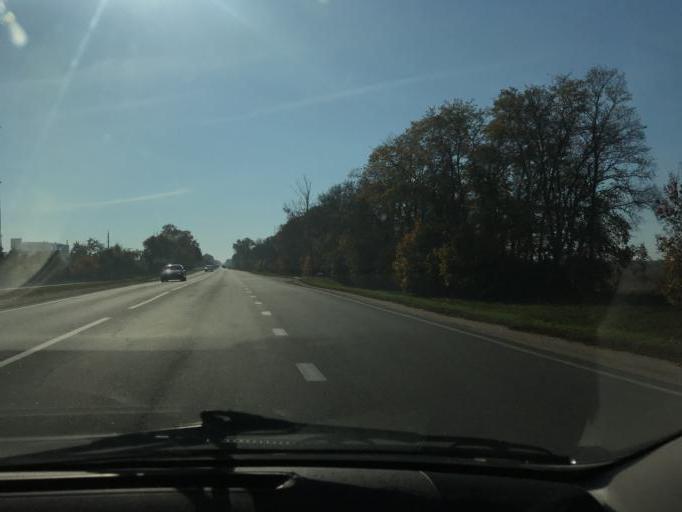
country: BY
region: Minsk
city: Starobin
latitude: 52.8000
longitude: 27.4646
